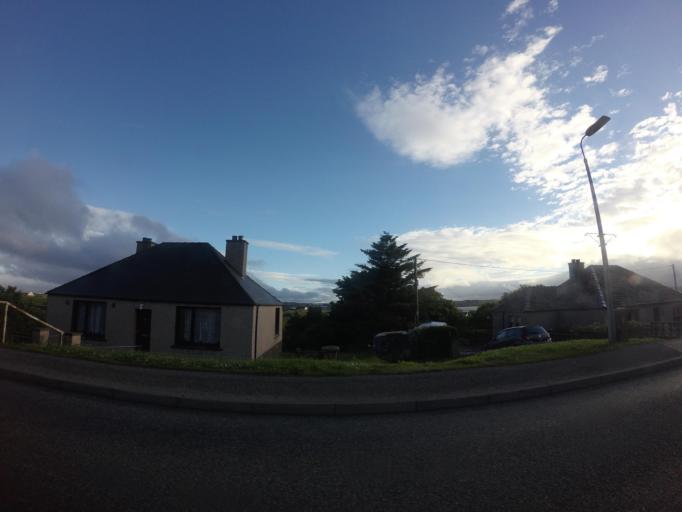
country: GB
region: Scotland
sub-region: Eilean Siar
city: Stornoway
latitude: 58.2039
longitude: -6.3512
